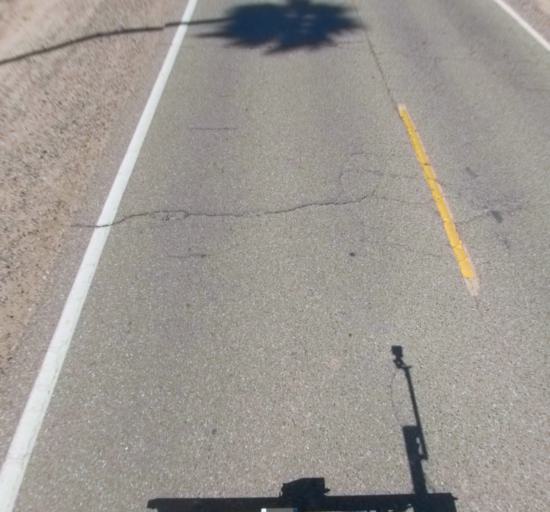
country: US
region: California
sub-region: Madera County
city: Chowchilla
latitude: 37.0440
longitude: -120.3311
